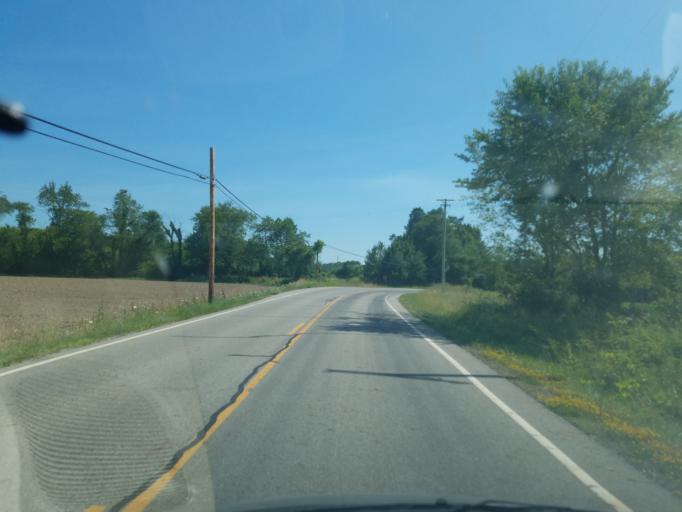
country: US
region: Ohio
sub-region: Geauga County
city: Burton
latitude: 41.4568
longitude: -81.1546
